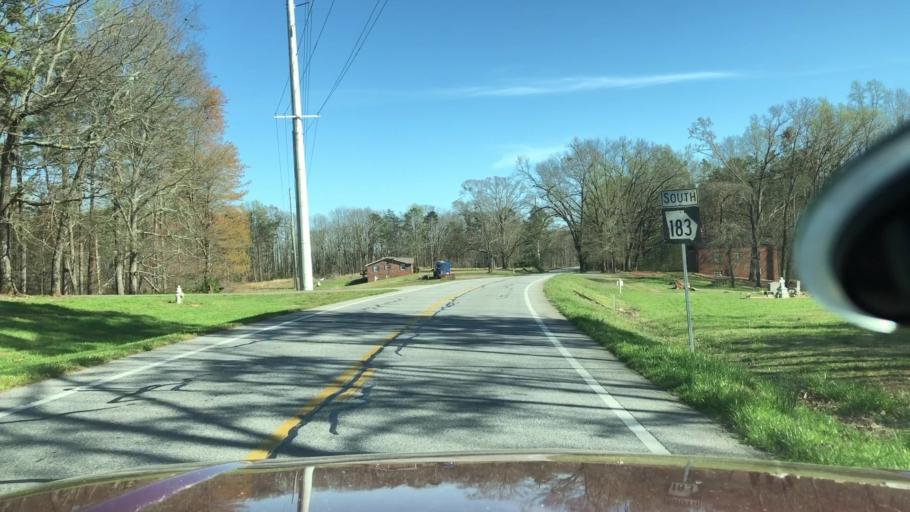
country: US
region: Georgia
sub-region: Dawson County
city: Dawsonville
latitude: 34.4655
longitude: -84.1773
